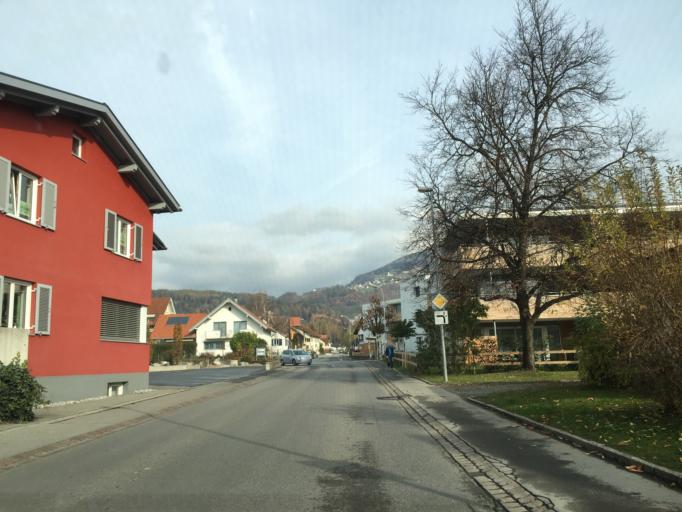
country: AT
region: Vorarlberg
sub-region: Politischer Bezirk Feldkirch
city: Sulz
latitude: 47.2827
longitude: 9.6584
